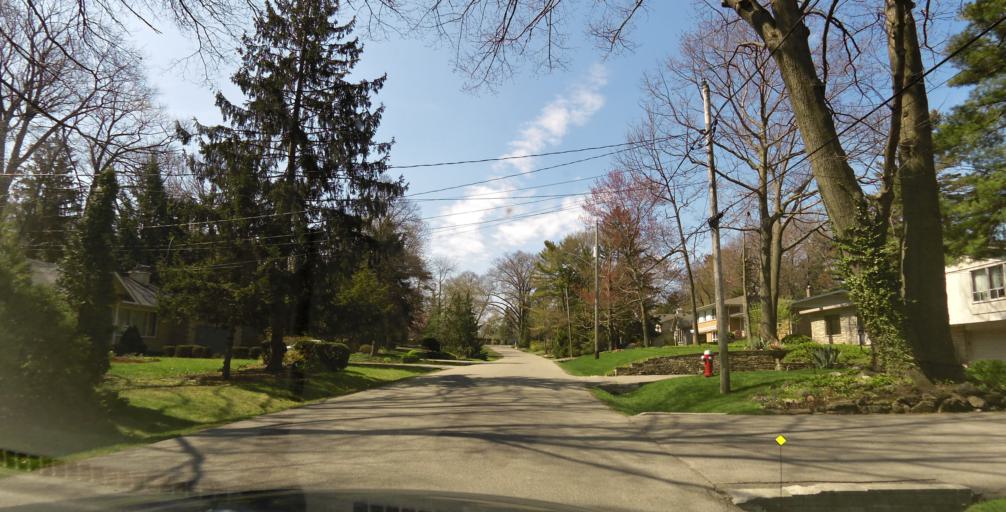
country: CA
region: Ontario
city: Mississauga
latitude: 43.5529
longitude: -79.6037
